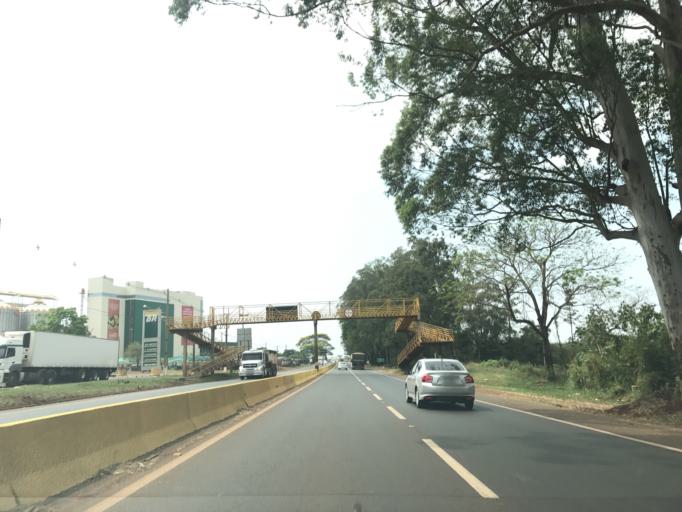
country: BR
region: Parana
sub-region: Rolandia
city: Rolandia
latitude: -23.3569
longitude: -51.3948
